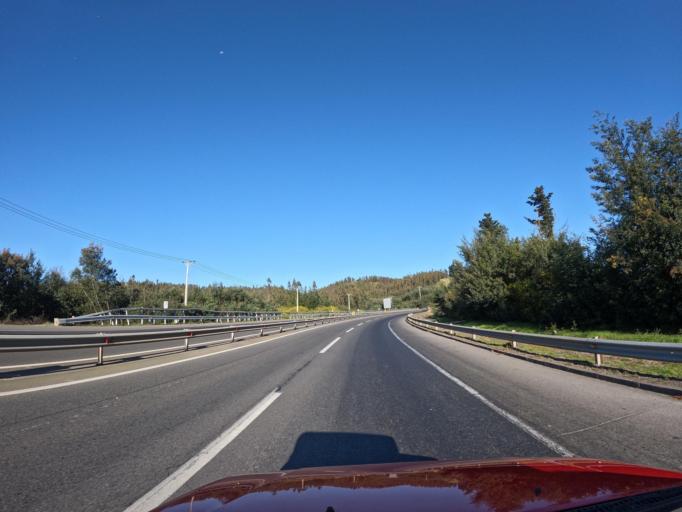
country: CL
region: Biobio
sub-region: Provincia de Concepcion
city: Penco
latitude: -36.7541
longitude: -72.9798
